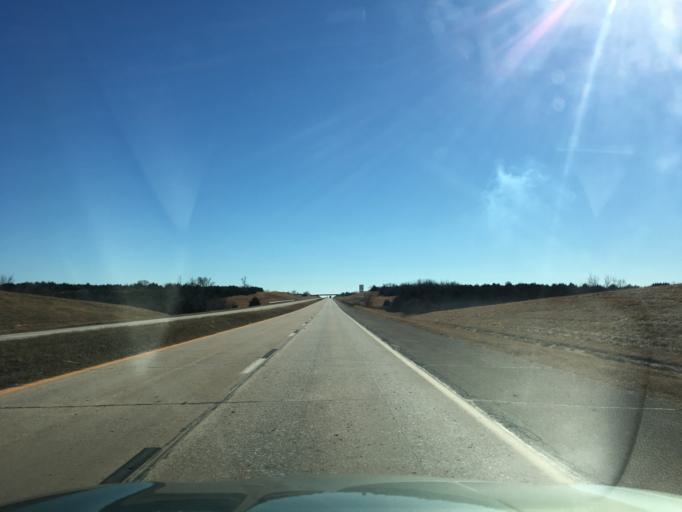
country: US
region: Oklahoma
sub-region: Pawnee County
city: Pawnee
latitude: 36.2884
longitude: -96.9834
